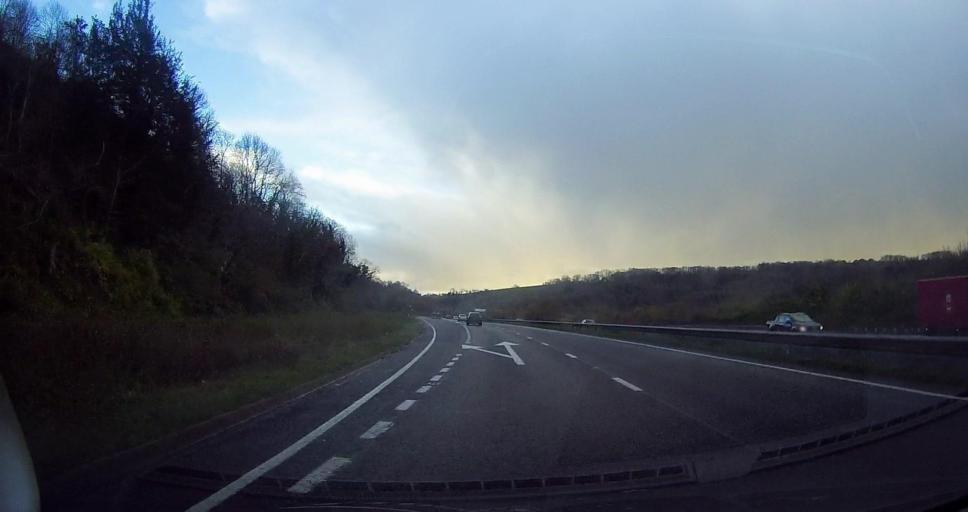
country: GB
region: England
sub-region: West Sussex
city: Hurstpierpoint
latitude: 50.9084
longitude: -0.1903
